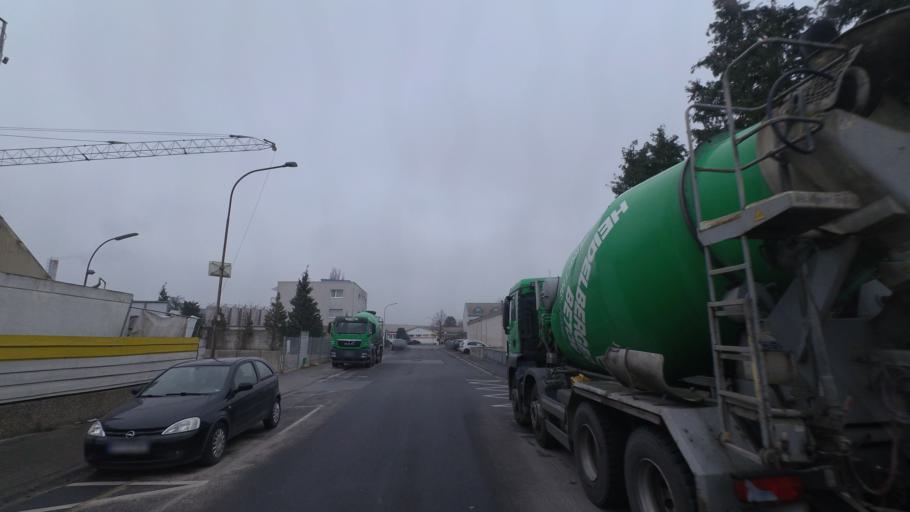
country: DE
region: Hesse
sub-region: Regierungsbezirk Darmstadt
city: Seligenstadt
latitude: 50.0657
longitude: 8.9675
